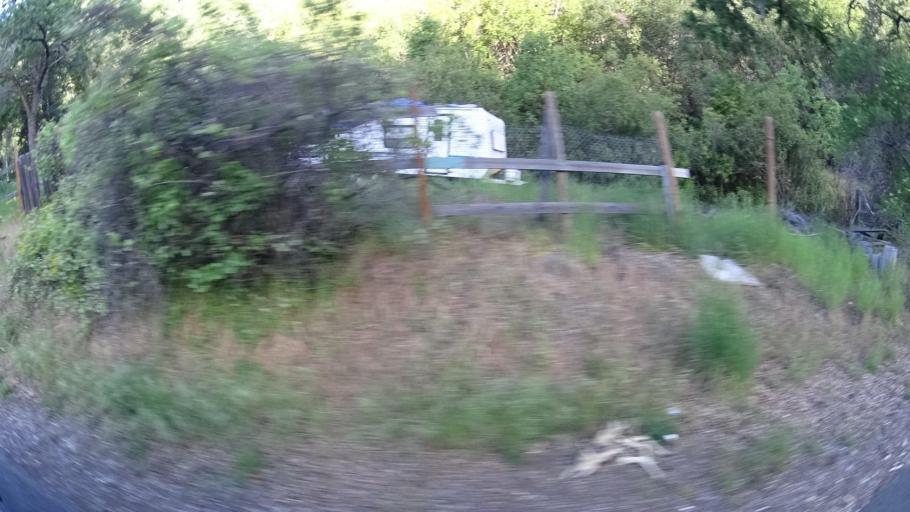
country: US
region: California
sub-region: Lake County
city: Upper Lake
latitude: 39.1510
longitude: -122.9997
